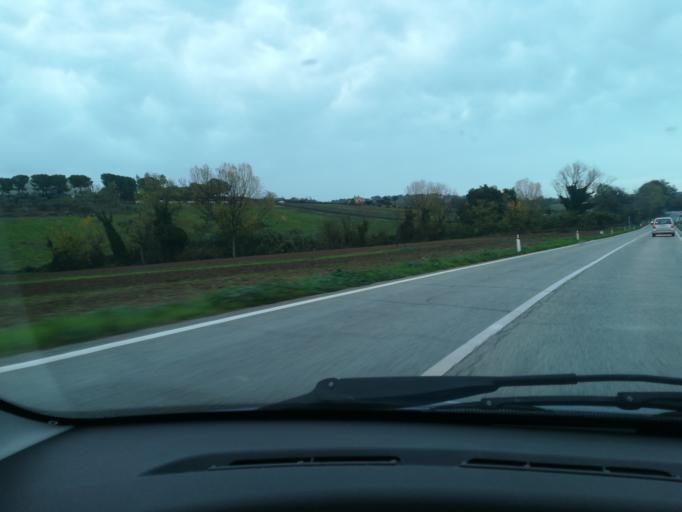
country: IT
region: The Marches
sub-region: Provincia di Macerata
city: Borgo Stazione
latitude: 43.2939
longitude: 13.6650
